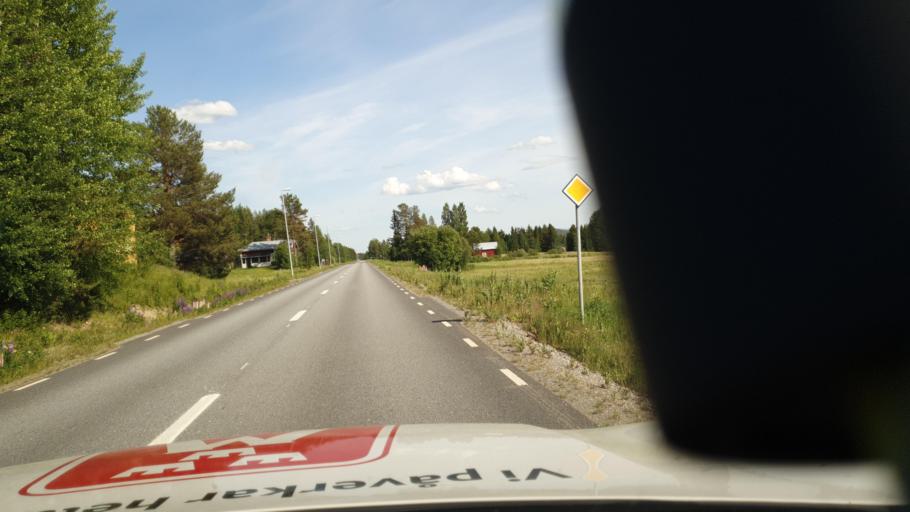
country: SE
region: Vaesterbotten
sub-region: Skelleftea Kommun
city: Forsbacka
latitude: 64.7034
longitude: 20.4484
